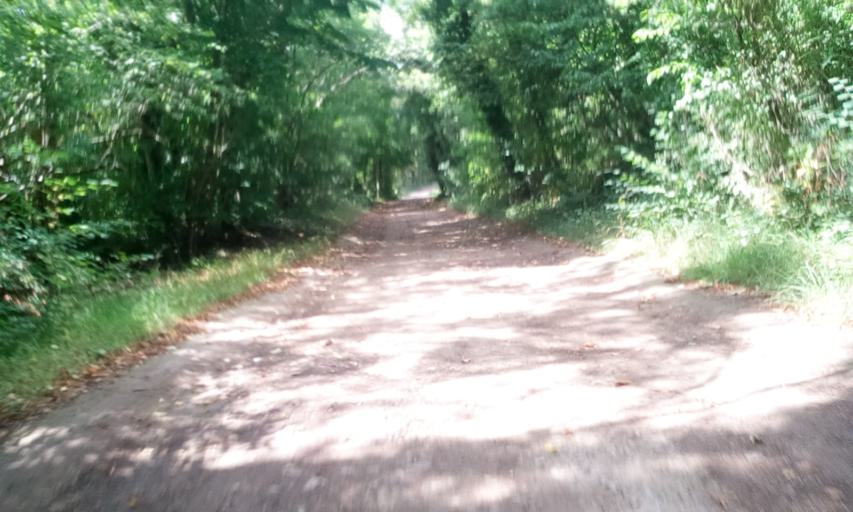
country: FR
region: Lower Normandy
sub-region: Departement du Calvados
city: Bourguebus
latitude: 49.1033
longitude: -0.2619
